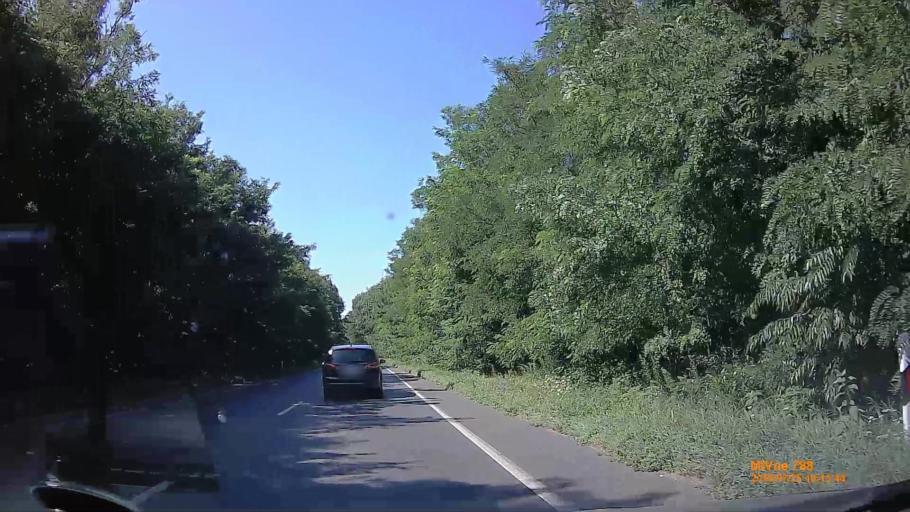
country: HU
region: Szabolcs-Szatmar-Bereg
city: Nyiregyhaza
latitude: 47.9881
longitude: 21.7216
